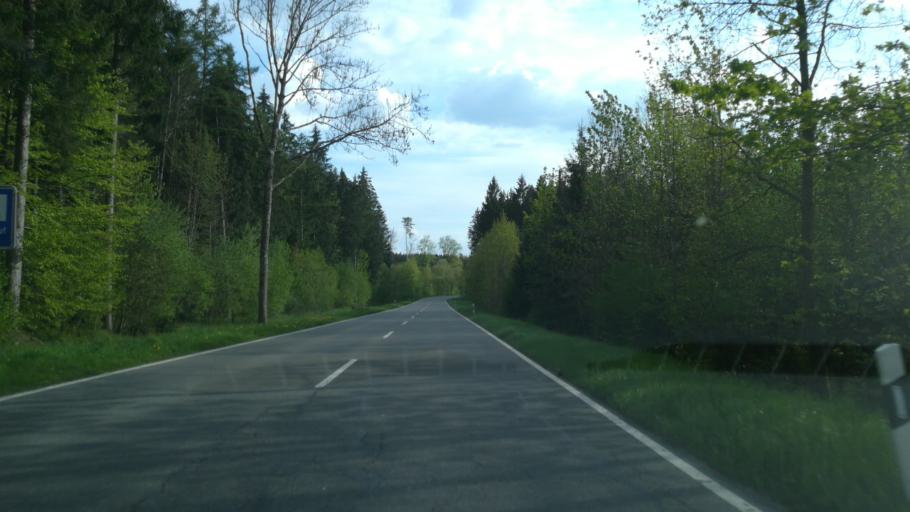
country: DE
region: Baden-Wuerttemberg
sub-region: Tuebingen Region
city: Messkirch
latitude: 47.9755
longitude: 9.0794
